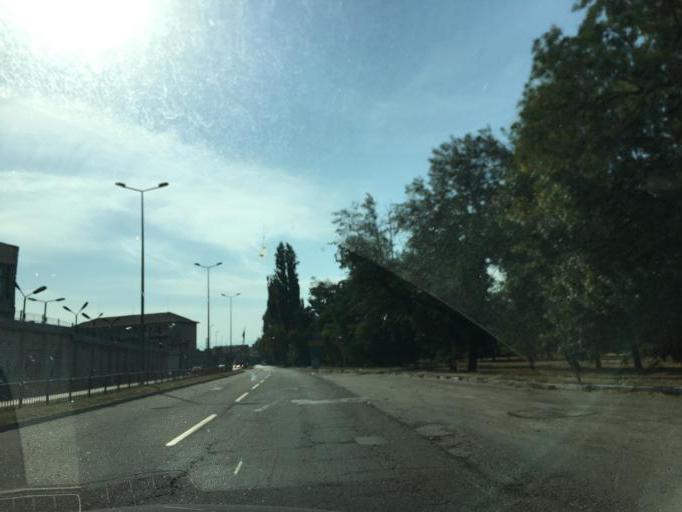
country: BG
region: Pazardzhik
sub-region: Obshtina Pazardzhik
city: Pazardzhik
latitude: 42.2108
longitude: 24.3240
